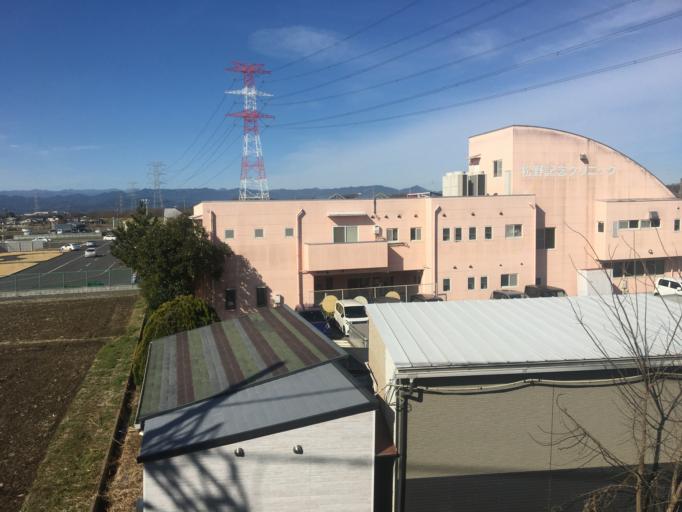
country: JP
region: Saitama
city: Sakado
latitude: 35.9831
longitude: 139.4006
